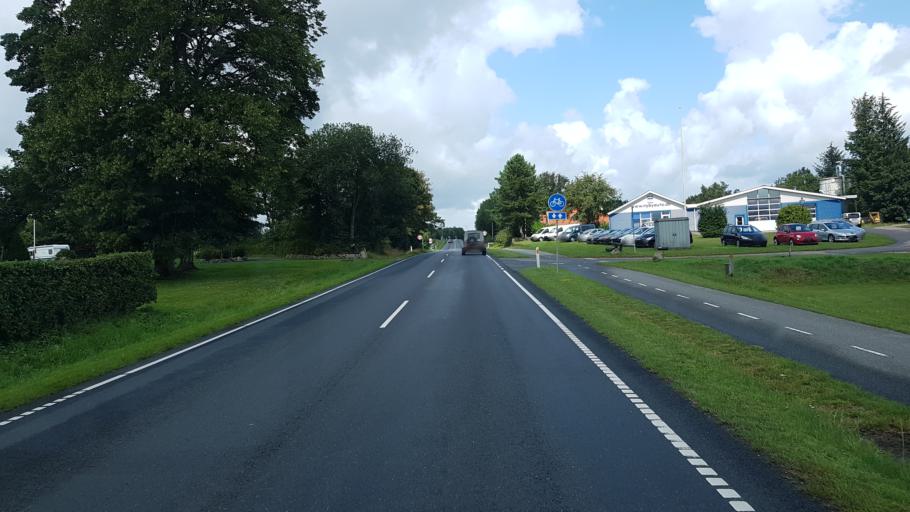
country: DK
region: South Denmark
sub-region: Vejen Kommune
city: Vejen
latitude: 55.5192
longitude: 9.1213
